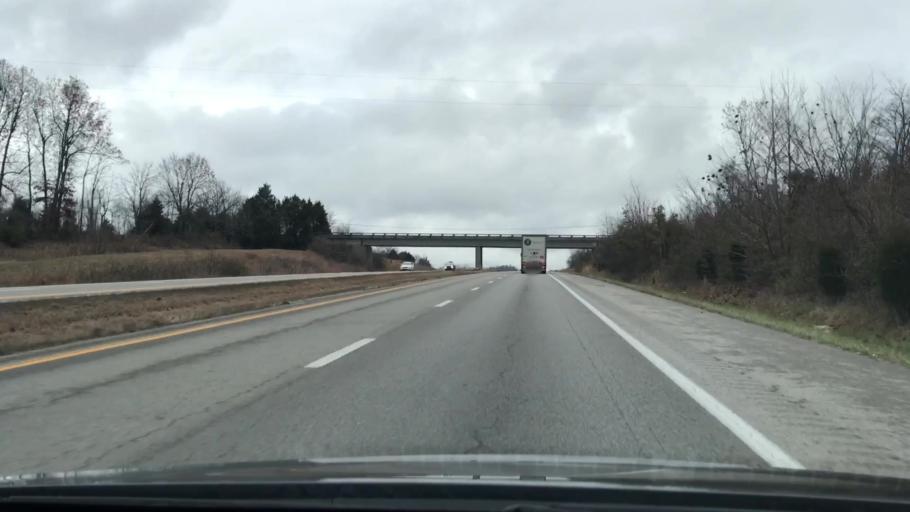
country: US
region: Kentucky
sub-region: Christian County
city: Hopkinsville
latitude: 36.9224
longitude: -87.4727
